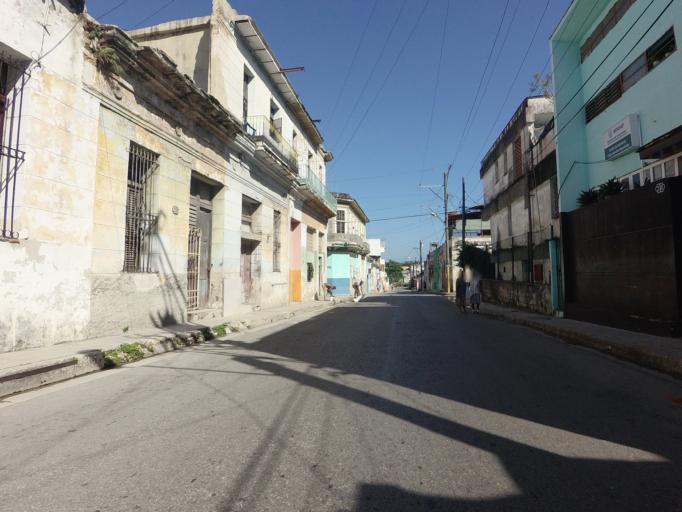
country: CU
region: La Habana
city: Cerro
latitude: 23.1196
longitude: -82.3736
